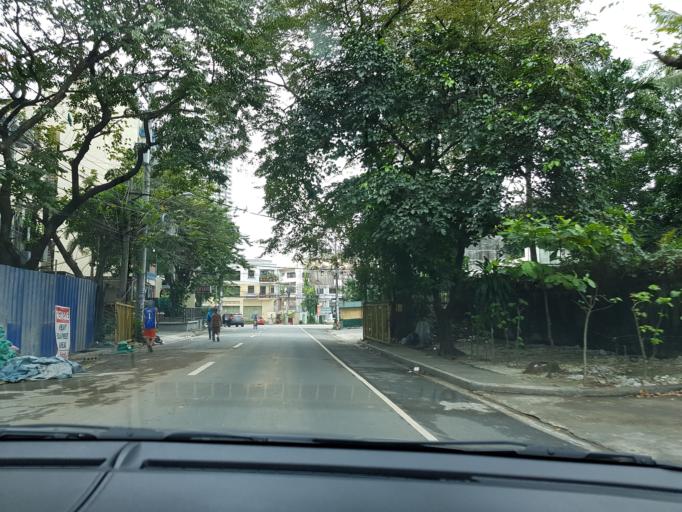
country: PH
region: Metro Manila
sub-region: Quezon City
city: Quezon City
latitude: 14.6390
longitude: 121.0391
